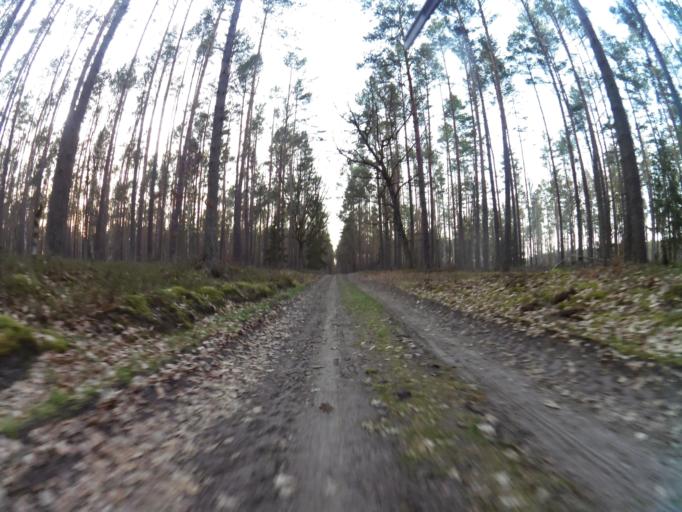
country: PL
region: West Pomeranian Voivodeship
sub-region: Powiat policki
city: Nowe Warpno
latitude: 53.6920
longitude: 14.3283
